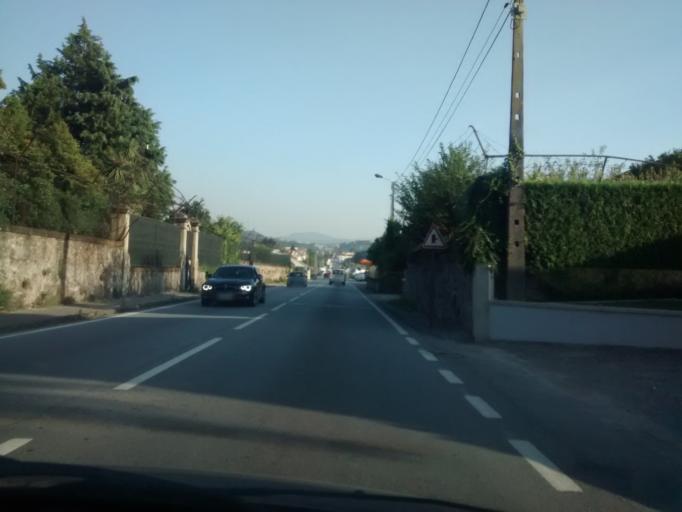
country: PT
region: Braga
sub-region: Braga
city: Adaufe
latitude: 41.5836
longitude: -8.4288
